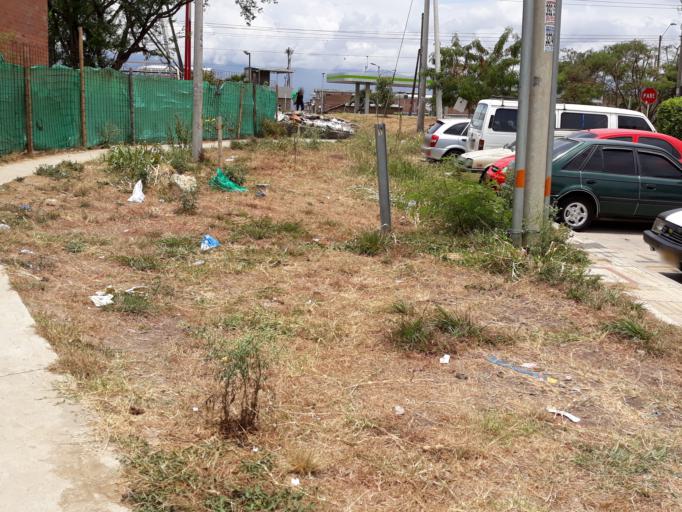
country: CO
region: Valle del Cauca
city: Cali
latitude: 3.4279
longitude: -76.4765
